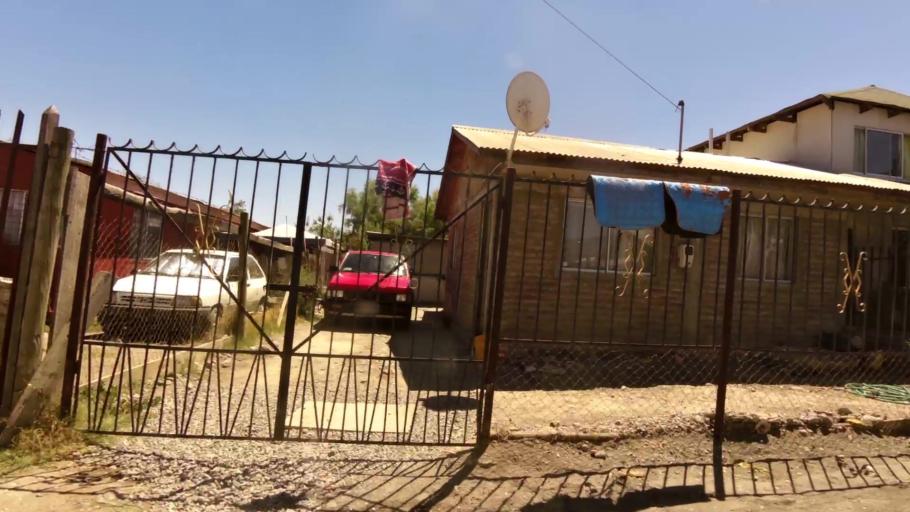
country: CL
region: O'Higgins
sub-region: Provincia de Cachapoal
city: Rancagua
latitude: -34.2180
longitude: -70.7813
